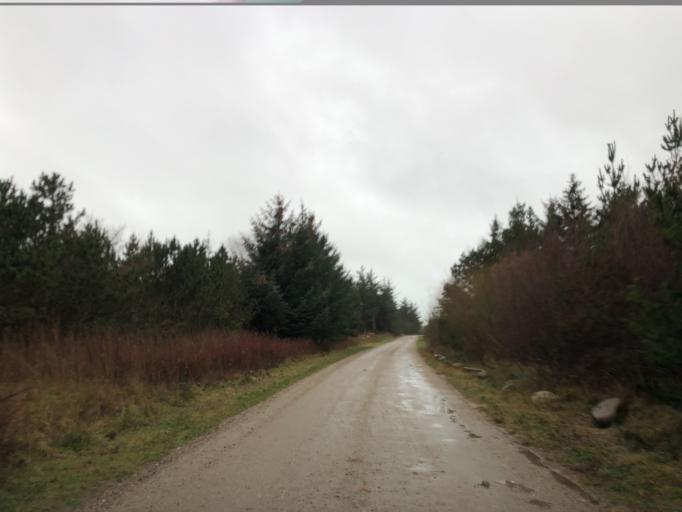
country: DK
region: Central Jutland
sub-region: Holstebro Kommune
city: Ulfborg
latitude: 56.2786
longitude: 8.1489
